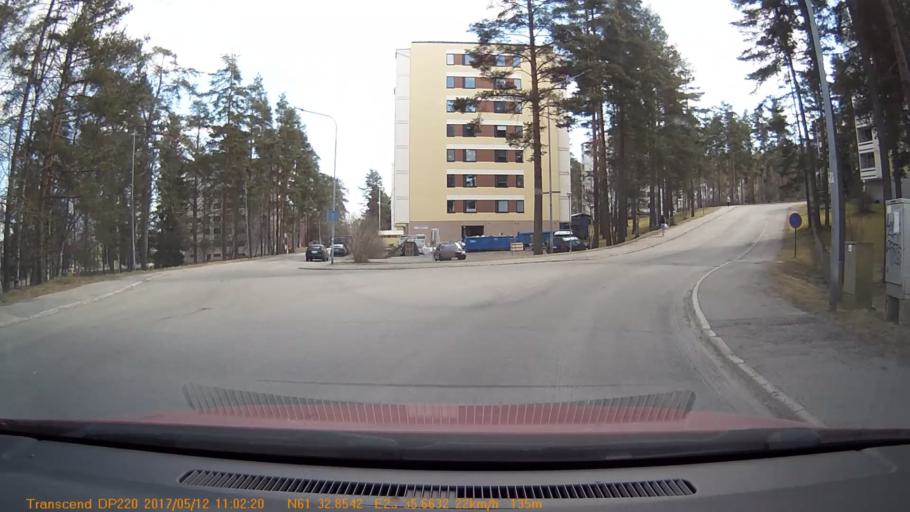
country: FI
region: Pirkanmaa
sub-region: Tampere
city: Yloejaervi
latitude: 61.5476
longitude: 23.5943
